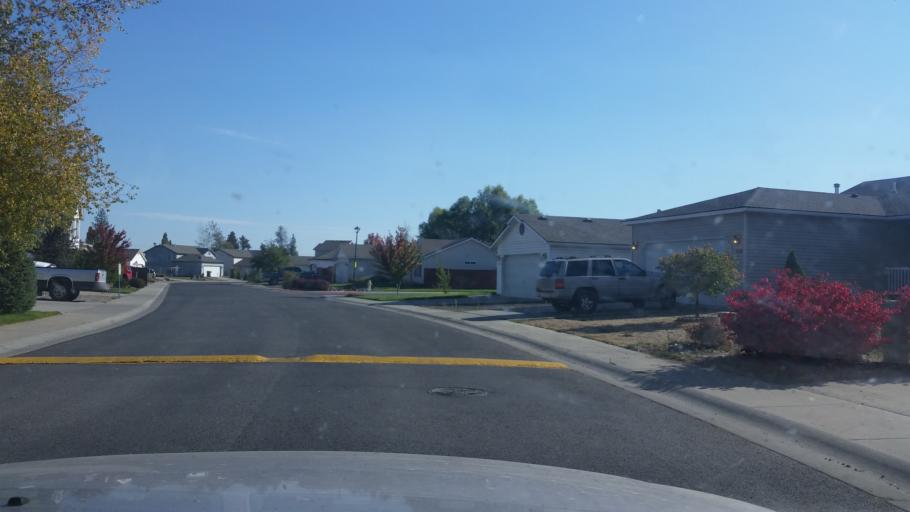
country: US
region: Washington
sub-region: Spokane County
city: Cheney
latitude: 47.5102
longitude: -117.5669
